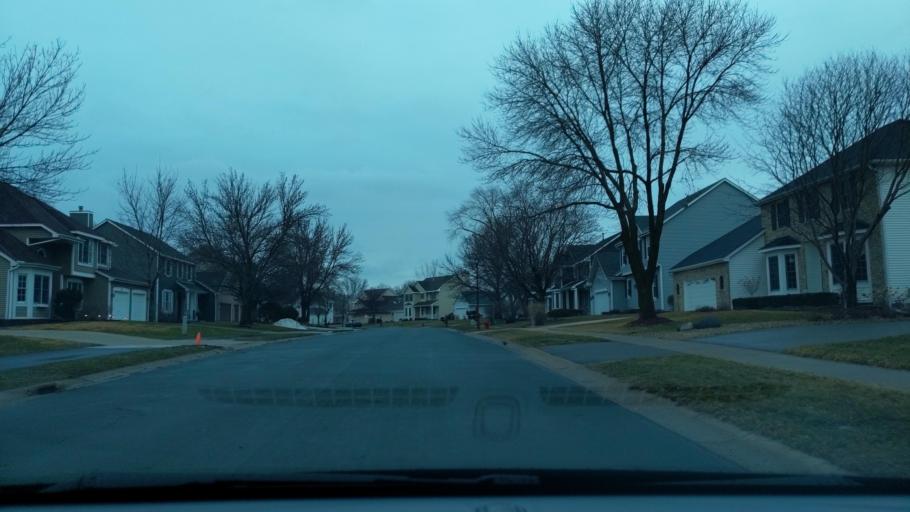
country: US
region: Minnesota
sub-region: Hennepin County
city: Eden Prairie
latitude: 44.8480
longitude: -93.4908
